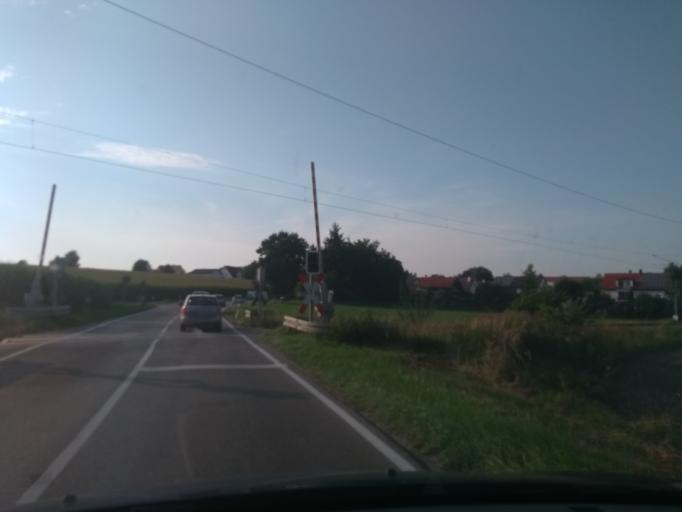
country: DE
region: Bavaria
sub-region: Upper Bavaria
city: Schwabhausen
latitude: 48.3166
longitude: 11.3882
